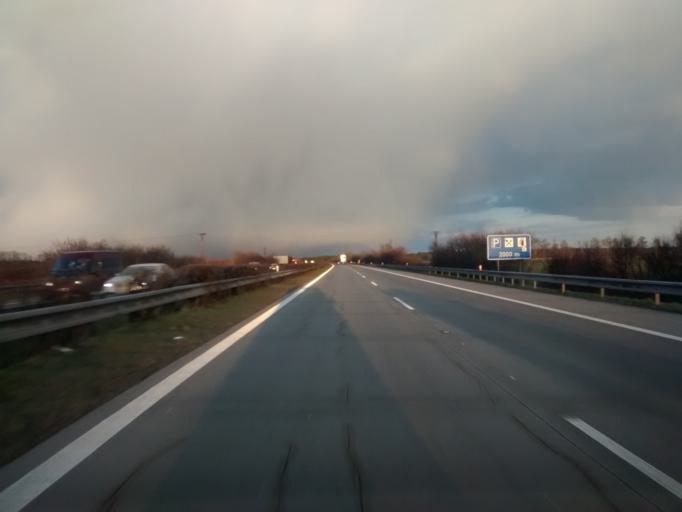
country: CZ
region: Central Bohemia
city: Pecky
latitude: 50.1220
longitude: 15.0523
